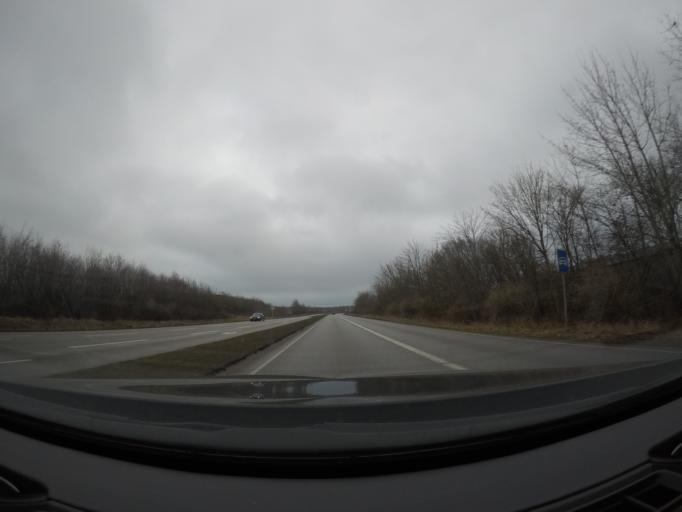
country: DK
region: South Denmark
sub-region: Kolding Kommune
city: Kolding
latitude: 55.5488
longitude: 9.5080
